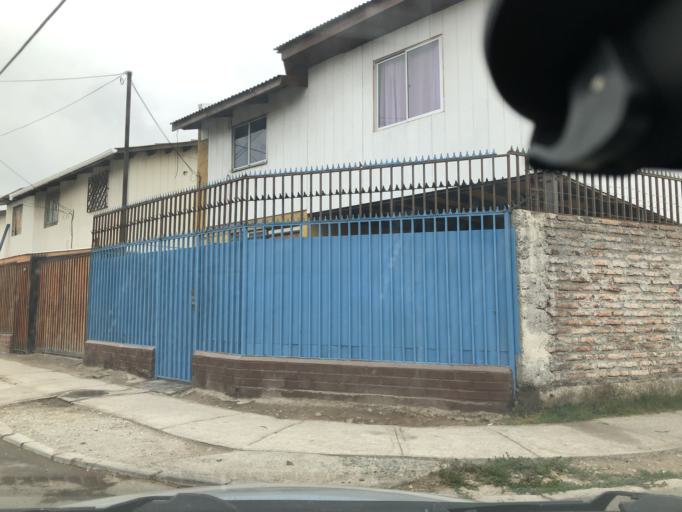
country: CL
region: Santiago Metropolitan
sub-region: Provincia de Santiago
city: La Pintana
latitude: -33.5718
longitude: -70.6080
